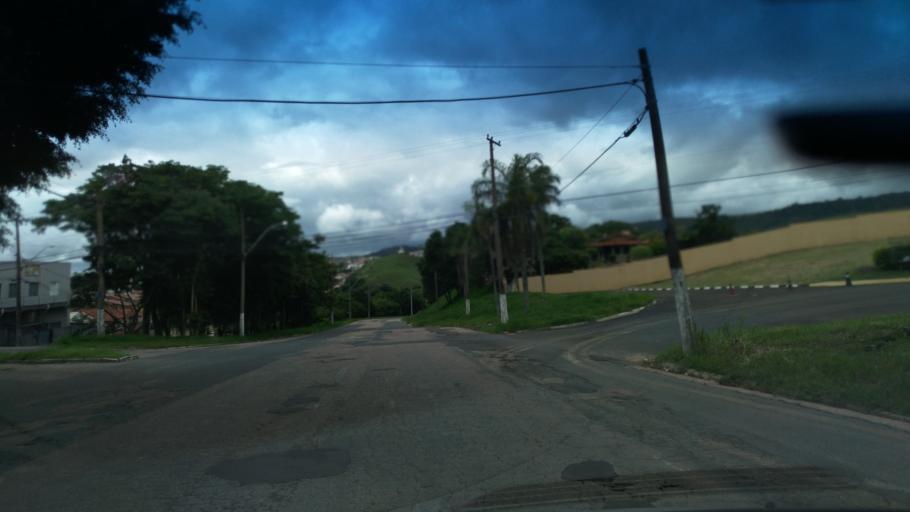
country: BR
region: Sao Paulo
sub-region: Valinhos
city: Valinhos
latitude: -22.9675
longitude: -46.9811
